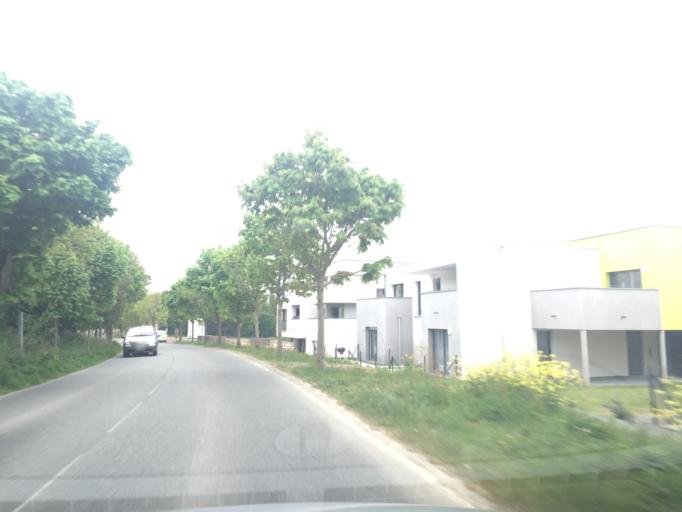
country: FR
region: Brittany
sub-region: Departement des Cotes-d'Armor
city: Paimpol
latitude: 48.7681
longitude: -3.0346
